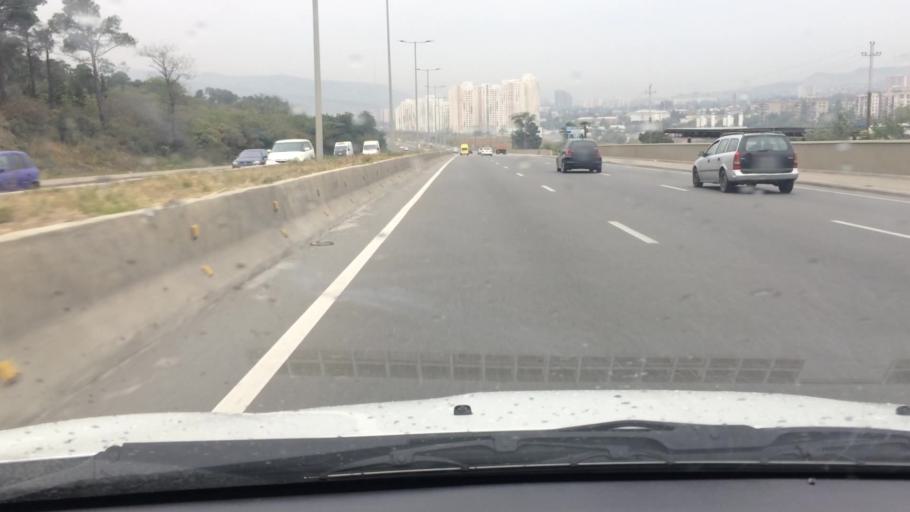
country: GE
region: T'bilisi
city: Tbilisi
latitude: 41.6655
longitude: 44.8694
